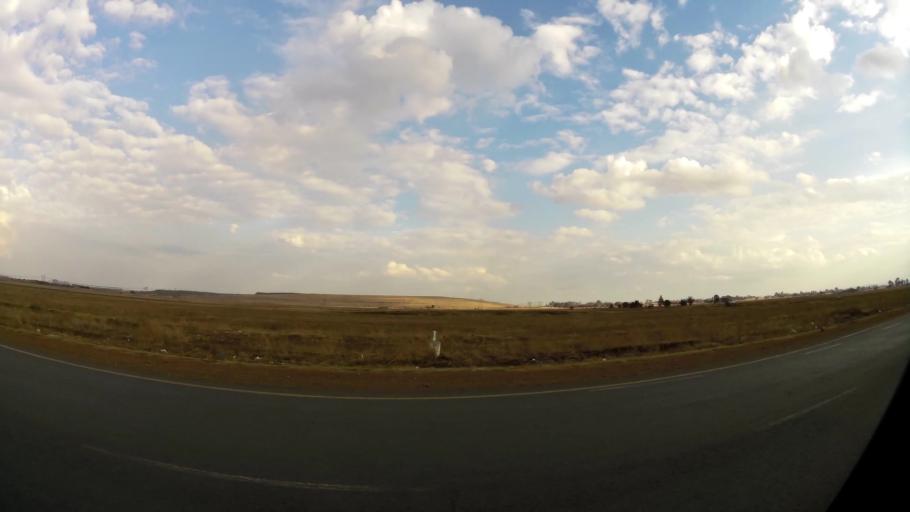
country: ZA
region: Gauteng
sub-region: Sedibeng District Municipality
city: Vanderbijlpark
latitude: -26.6197
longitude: 27.8140
